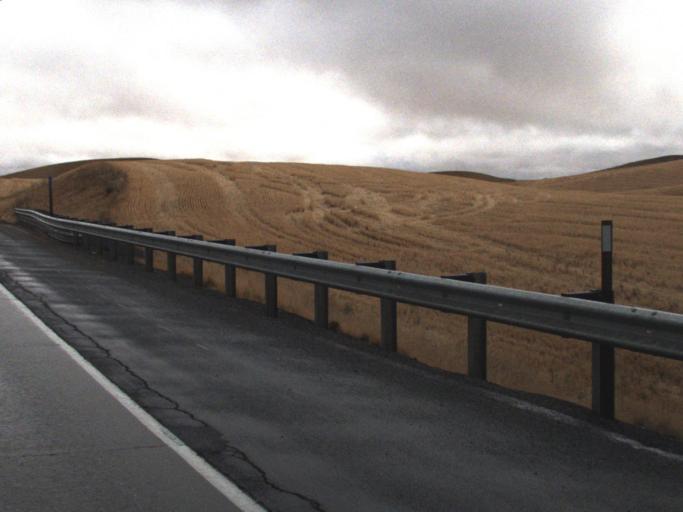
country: US
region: Washington
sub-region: Whitman County
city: Colfax
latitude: 47.1505
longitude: -117.3791
